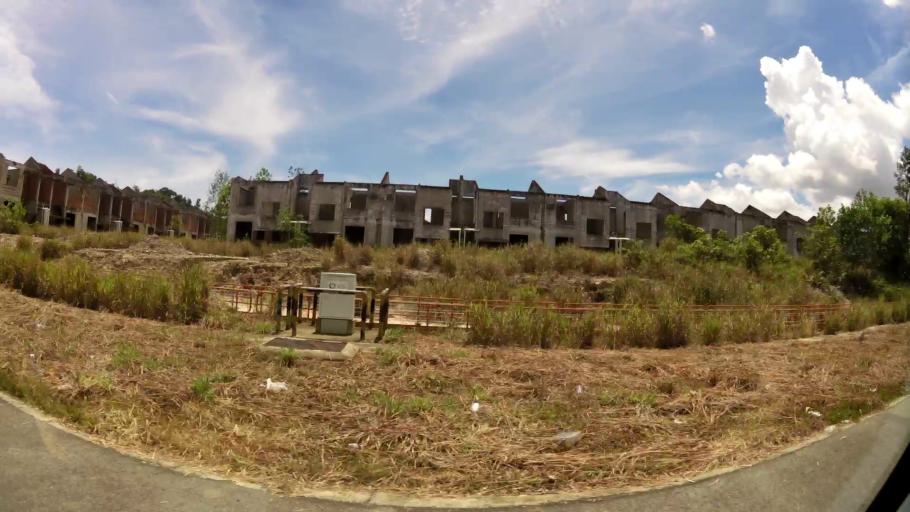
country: BN
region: Brunei and Muara
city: Bandar Seri Begawan
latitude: 4.9683
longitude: 114.9107
